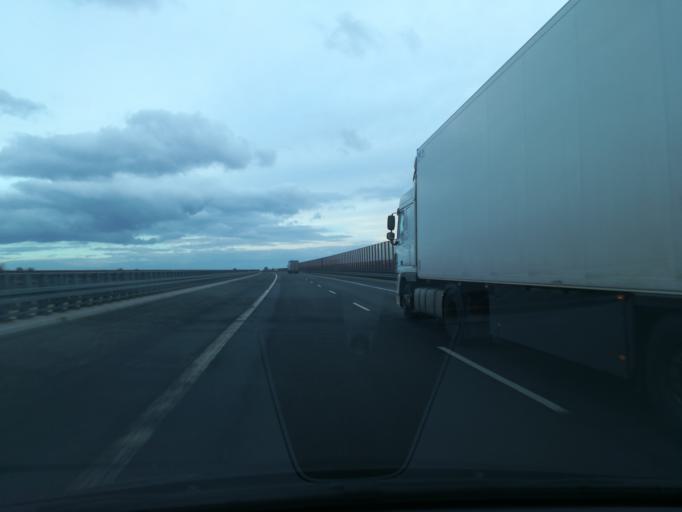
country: PL
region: Lodz Voivodeship
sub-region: Powiat kutnowski
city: Krzyzanow
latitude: 52.1393
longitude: 19.4839
